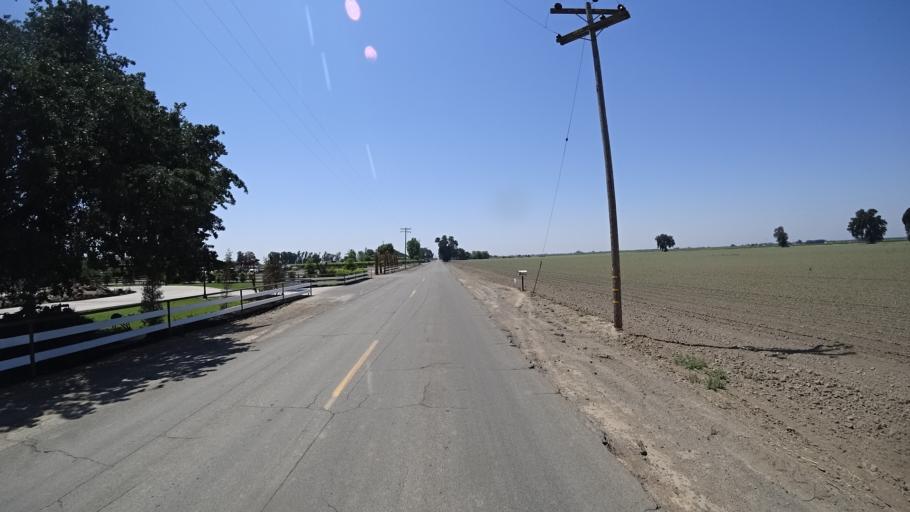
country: US
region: California
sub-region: Kings County
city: Armona
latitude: 36.3698
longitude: -119.7452
